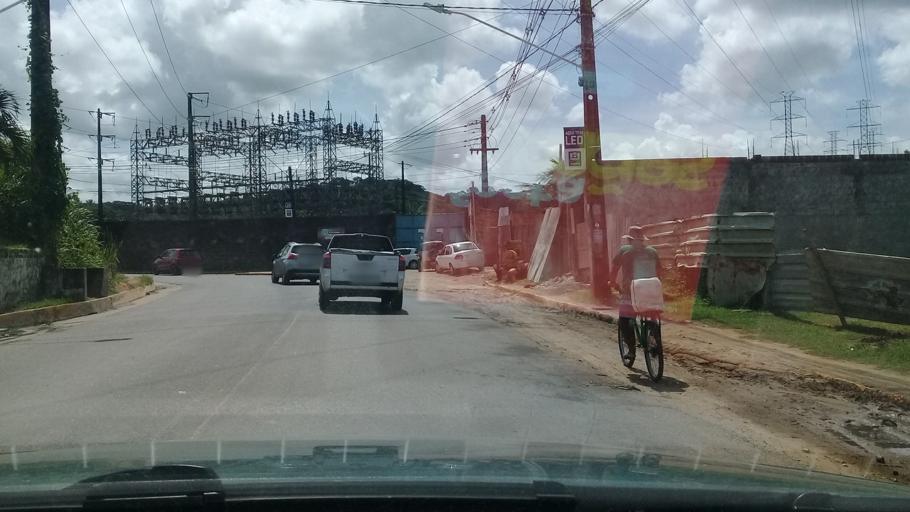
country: BR
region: Pernambuco
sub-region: Jaboatao Dos Guararapes
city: Jaboatao dos Guararapes
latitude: -8.0948
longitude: -35.0214
